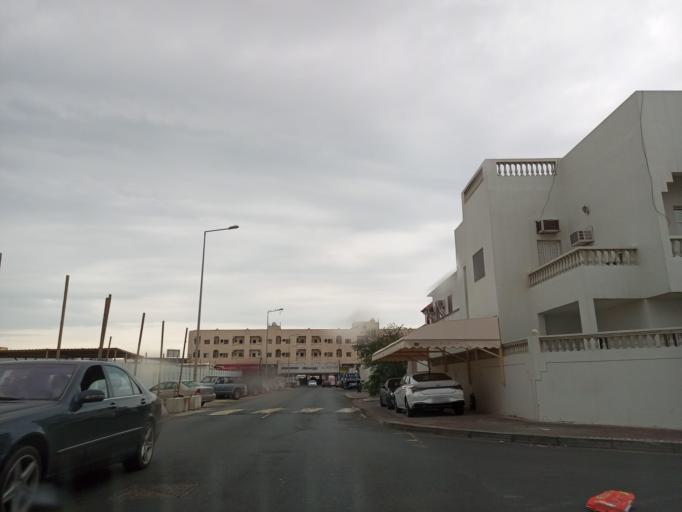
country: BH
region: Muharraq
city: Al Hadd
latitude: 26.2587
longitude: 50.6402
